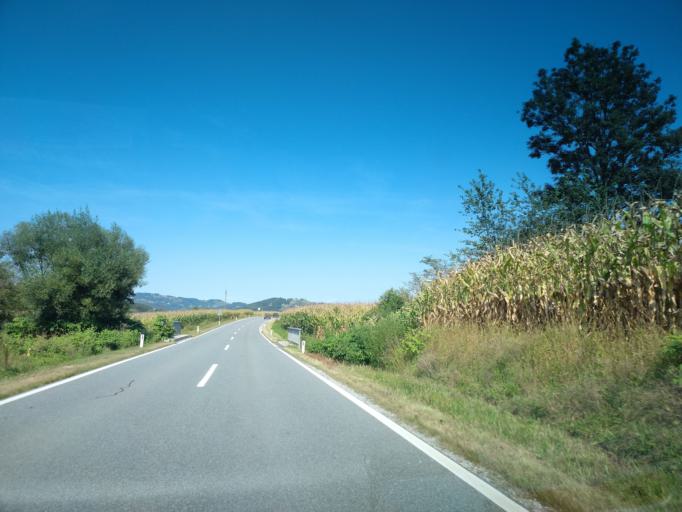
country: AT
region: Styria
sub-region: Politischer Bezirk Leibnitz
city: Sankt Johann im Saggautal
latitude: 46.7195
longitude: 15.4102
